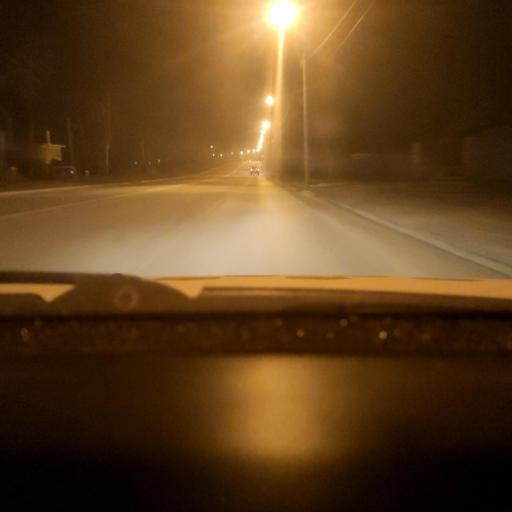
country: RU
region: Perm
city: Polazna
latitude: 58.1238
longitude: 56.4046
